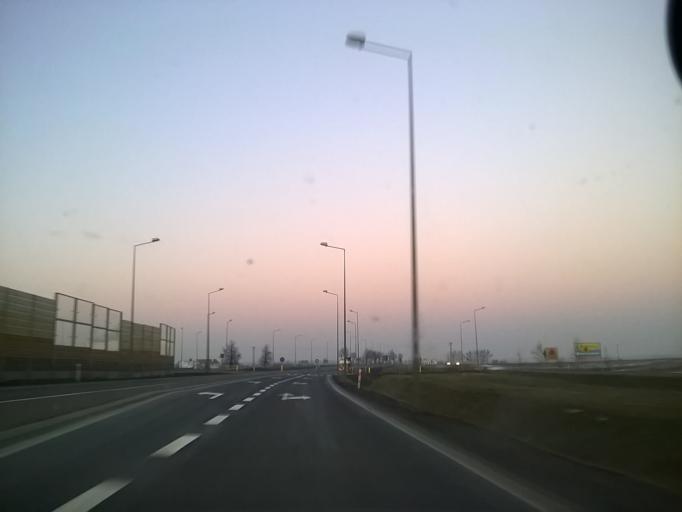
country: PL
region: Warmian-Masurian Voivodeship
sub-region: Powiat olsztynski
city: Barczewo
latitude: 53.8174
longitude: 20.6416
